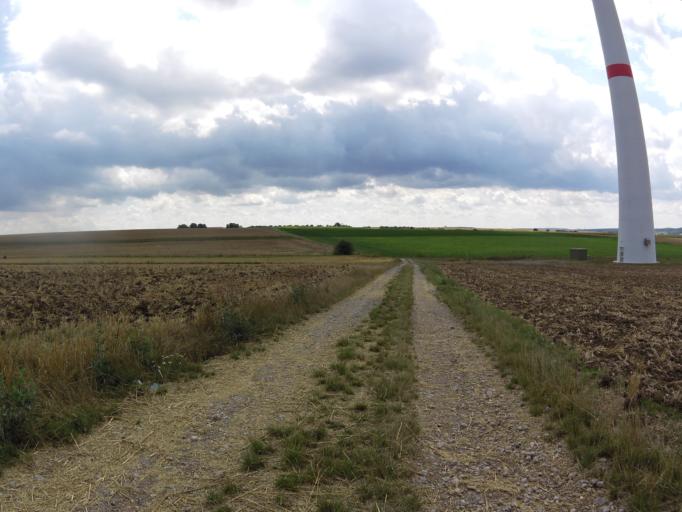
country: DE
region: Bavaria
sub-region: Regierungsbezirk Unterfranken
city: Geroldshausen
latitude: 49.6969
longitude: 9.8881
